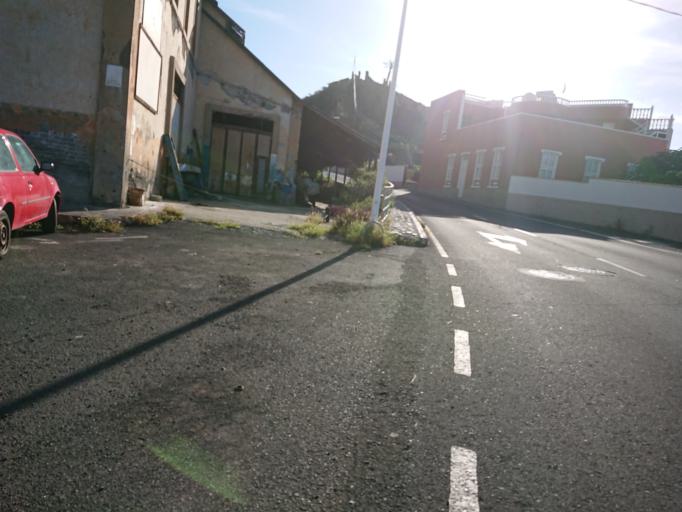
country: ES
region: Canary Islands
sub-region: Provincia de Santa Cruz de Tenerife
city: Tazacorte
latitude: 28.6479
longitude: -17.9438
